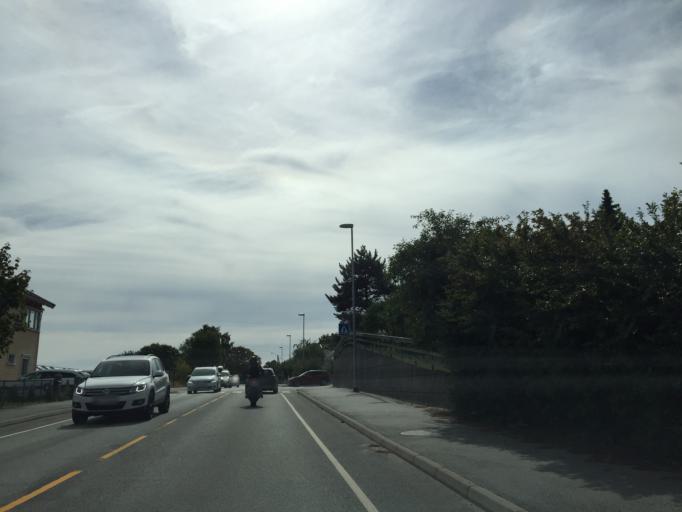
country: NO
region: Ostfold
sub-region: Fredrikstad
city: Fredrikstad
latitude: 59.2009
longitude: 10.9396
